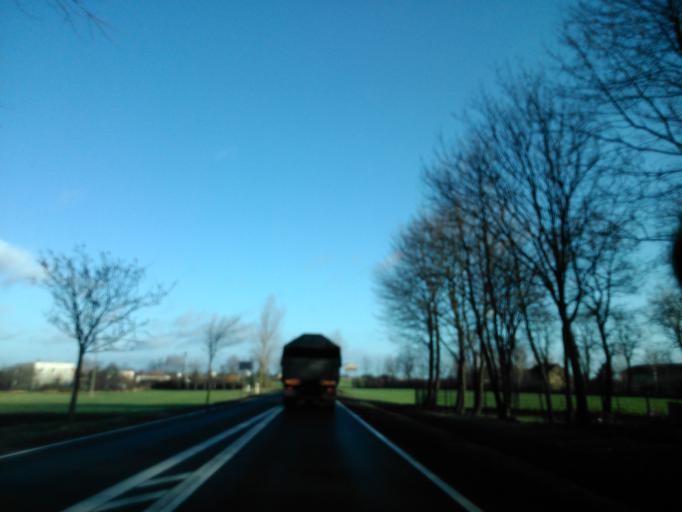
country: PL
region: Kujawsko-Pomorskie
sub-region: Powiat inowroclawski
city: Wierzchoslawice
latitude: 52.8498
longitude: 18.3431
